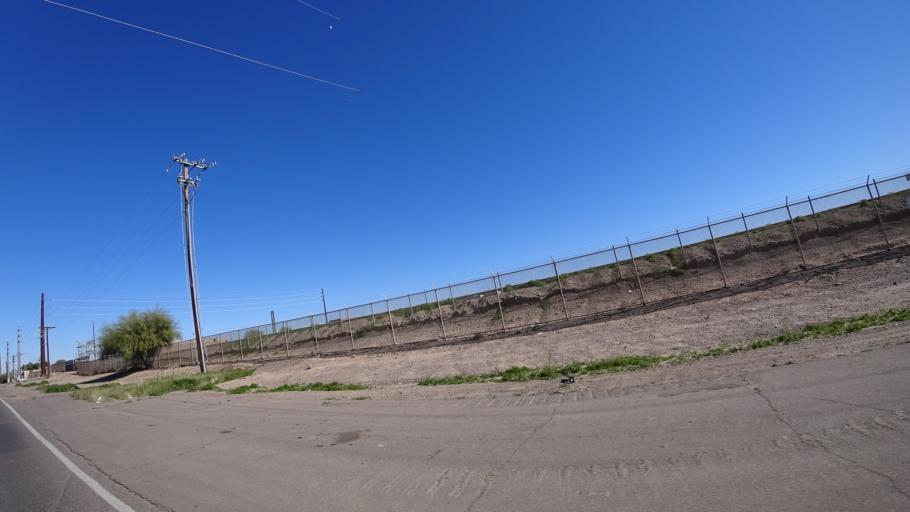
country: US
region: Arizona
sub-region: Maricopa County
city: Tolleson
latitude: 33.3907
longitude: -112.2543
